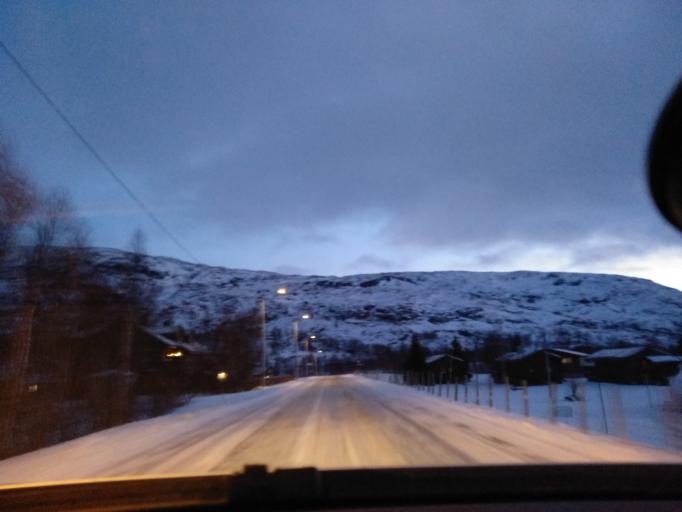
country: NO
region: Vest-Agder
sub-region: Sirdal
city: Tonstad
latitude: 59.0151
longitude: 6.9379
